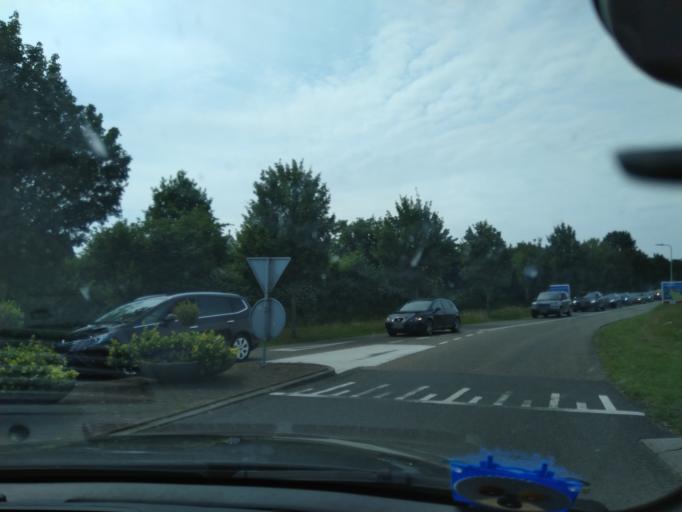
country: DE
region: Lower Saxony
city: Nordhorn
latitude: 52.3983
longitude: 7.0298
